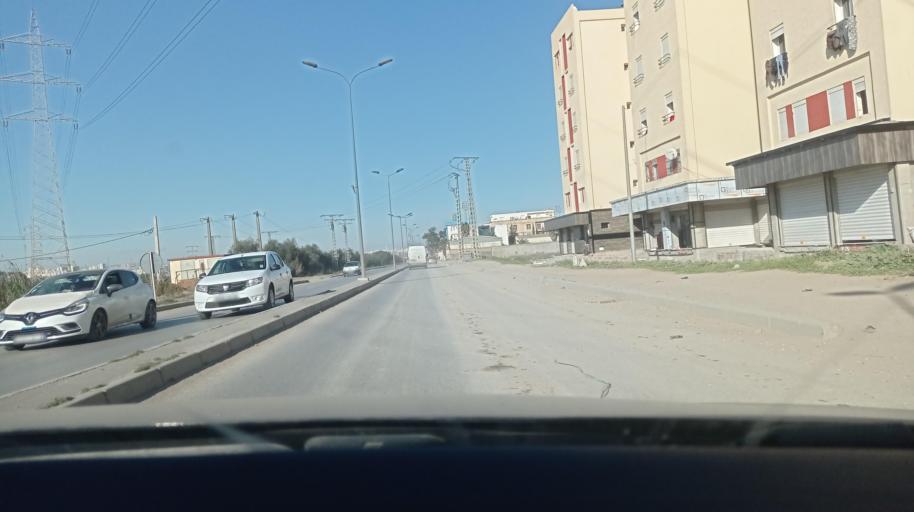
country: DZ
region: Tipaza
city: Baraki
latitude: 36.6637
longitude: 3.0855
